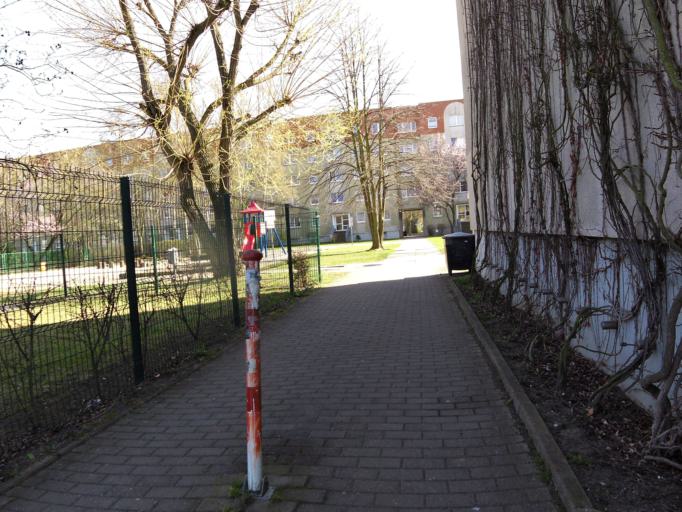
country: DE
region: Saxony
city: Leipzig
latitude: 51.3247
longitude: 12.2999
